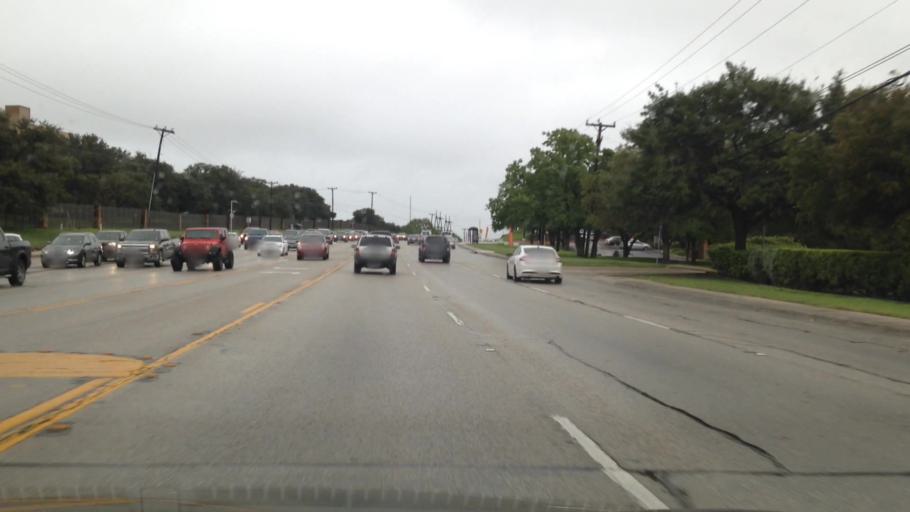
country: US
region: Texas
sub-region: Bexar County
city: Shavano Park
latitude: 29.5366
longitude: -98.5779
